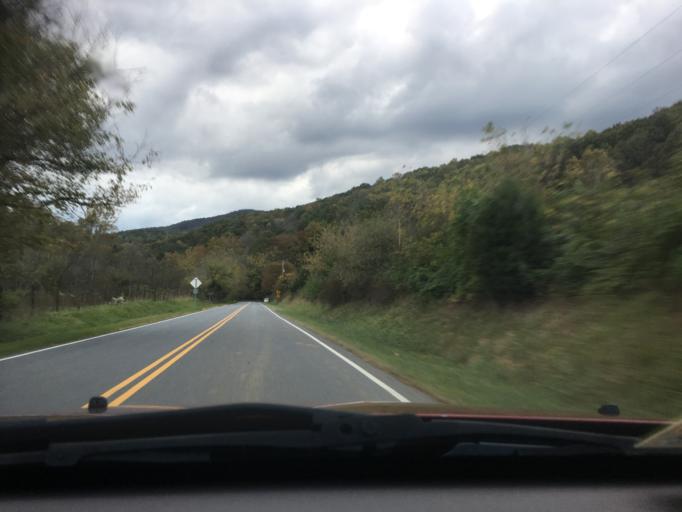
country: US
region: Virginia
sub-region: Giles County
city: Pearisburg
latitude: 37.2122
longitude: -80.7740
